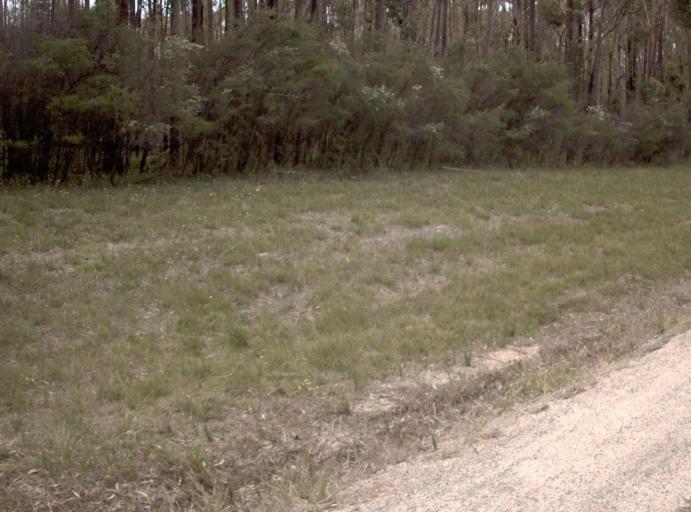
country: AU
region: New South Wales
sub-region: Bega Valley
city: Eden
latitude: -37.5383
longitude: 149.4705
